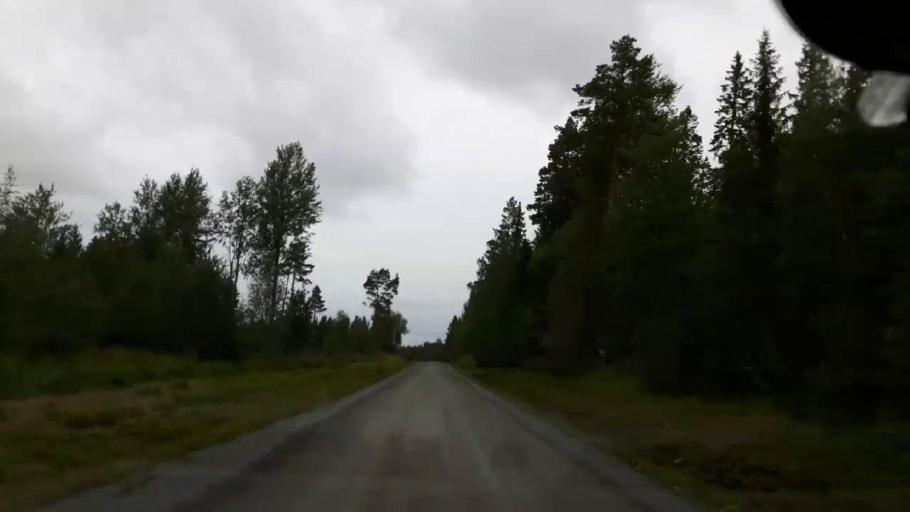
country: SE
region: Jaemtland
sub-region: OEstersunds Kommun
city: Ostersund
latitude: 63.1025
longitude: 14.5462
